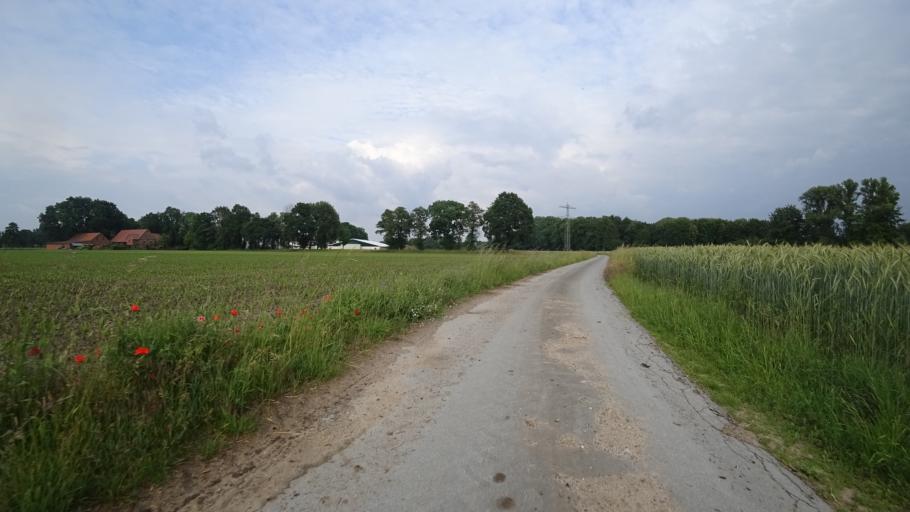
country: DE
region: North Rhine-Westphalia
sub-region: Regierungsbezirk Detmold
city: Guetersloh
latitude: 51.9435
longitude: 8.3742
